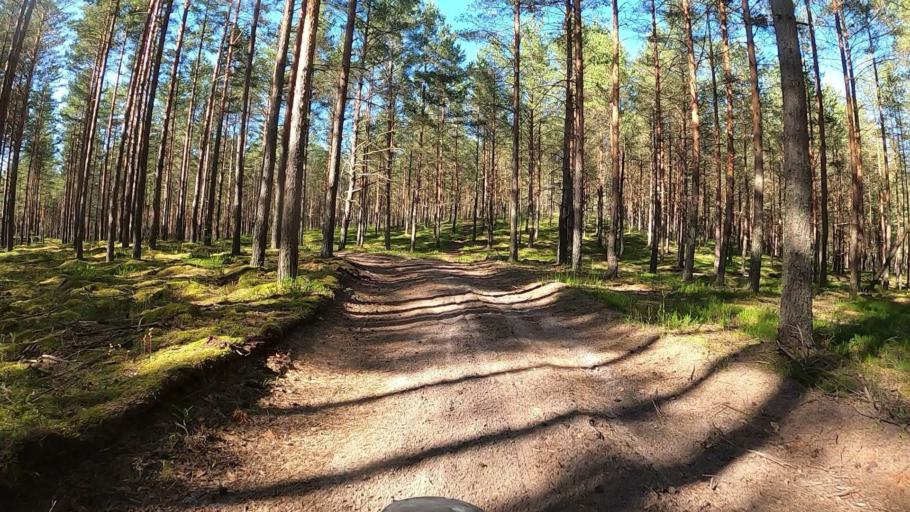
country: LV
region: Carnikava
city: Carnikava
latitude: 57.0898
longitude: 24.2561
